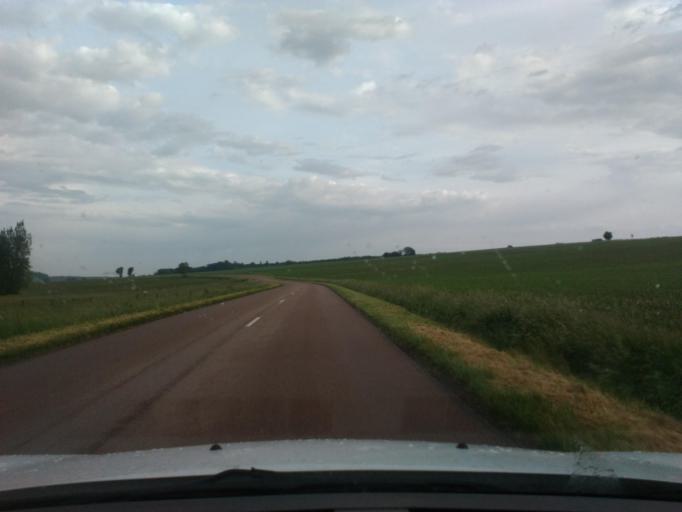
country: FR
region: Lorraine
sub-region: Departement des Vosges
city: Rambervillers
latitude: 48.3904
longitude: 6.5981
